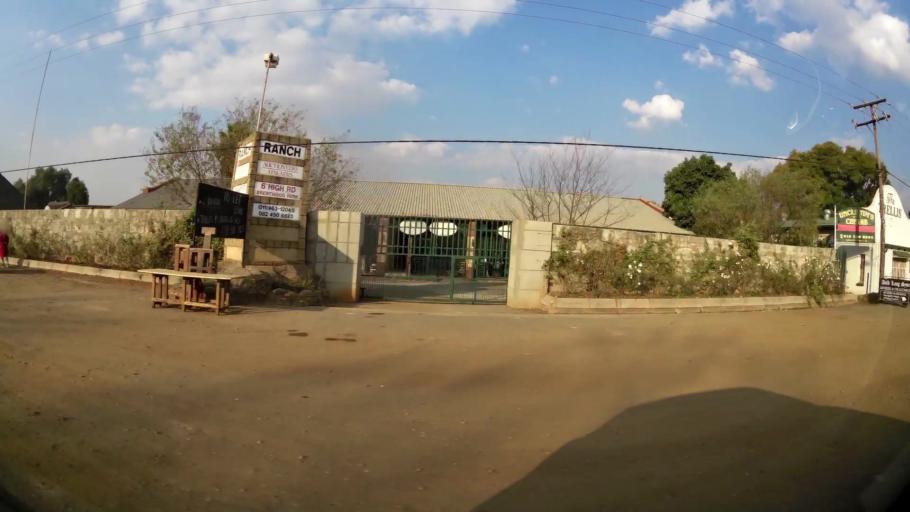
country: ZA
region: Gauteng
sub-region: Ekurhuleni Metropolitan Municipality
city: Benoni
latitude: -26.1224
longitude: 28.2938
